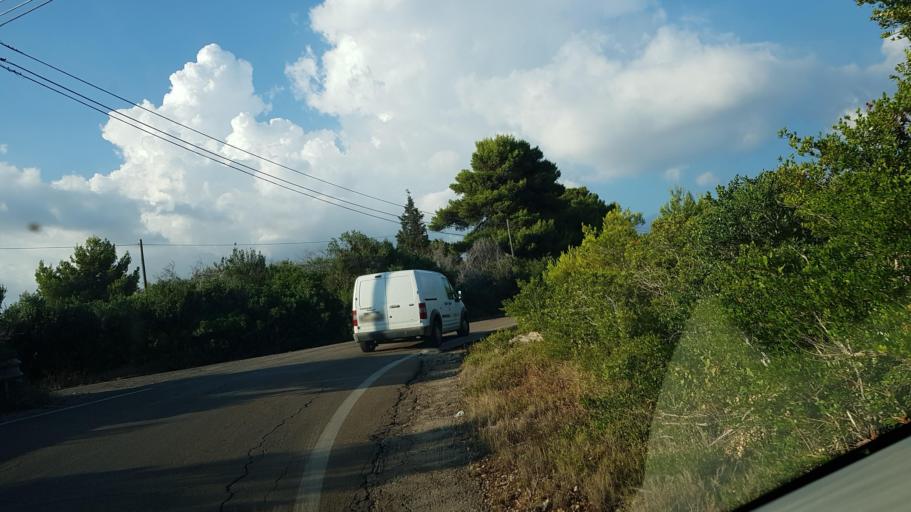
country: IT
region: Apulia
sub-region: Provincia di Lecce
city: Gemini
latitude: 39.8581
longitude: 18.2032
